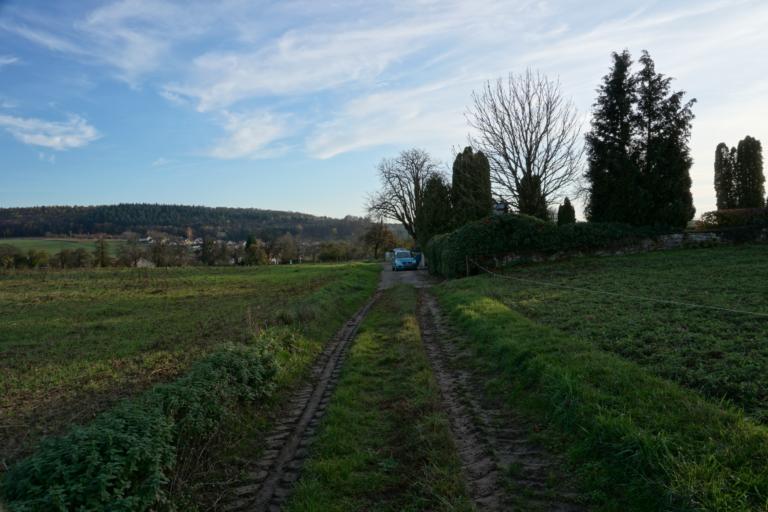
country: DE
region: Baden-Wuerttemberg
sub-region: Karlsruhe Region
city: Neunkirchen
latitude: 49.3700
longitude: 9.0222
